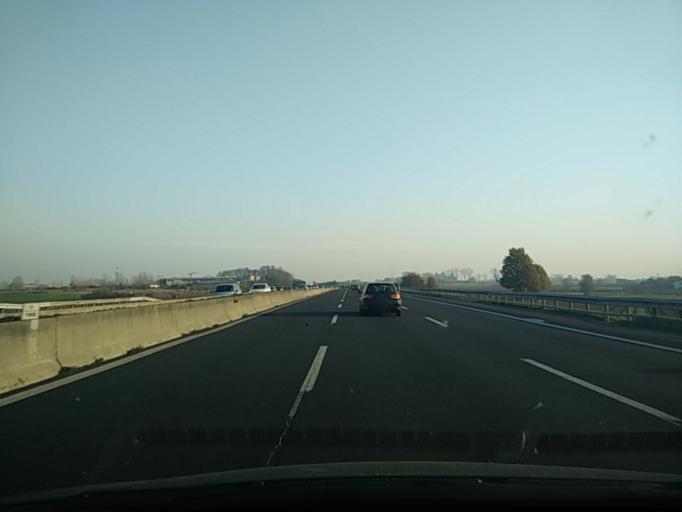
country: IT
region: Lombardy
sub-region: Provincia di Brescia
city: Villa Pedergnano
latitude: 45.5845
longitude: 9.9815
